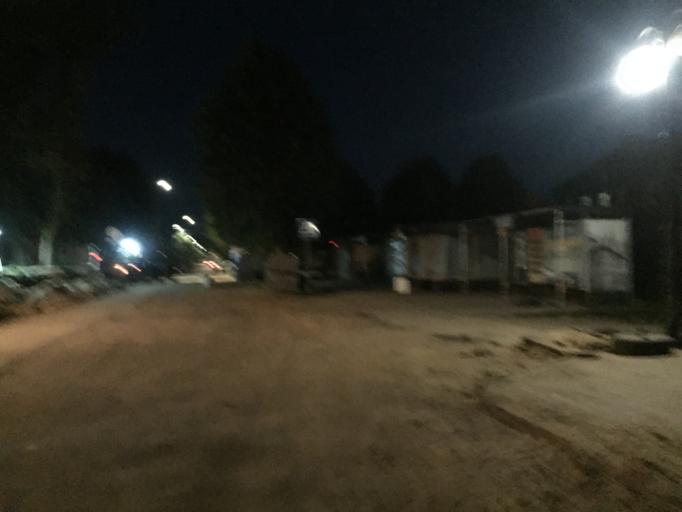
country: RU
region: Kaliningrad
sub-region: Gorod Kaliningrad
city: Yantarnyy
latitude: 54.8747
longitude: 19.9373
